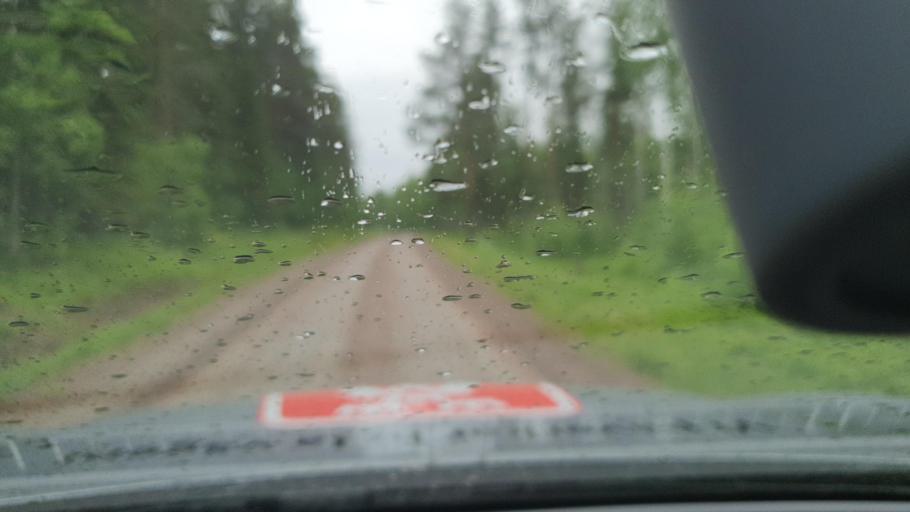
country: SE
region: Norrbotten
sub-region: Overkalix Kommun
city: OEverkalix
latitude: 66.5193
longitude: 22.7444
